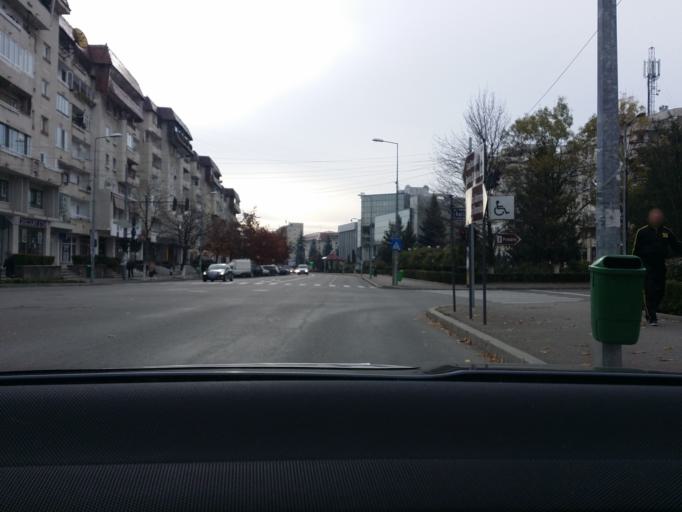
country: RO
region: Prahova
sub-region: Municipiul Campina
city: Campina
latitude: 45.1260
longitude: 25.7332
